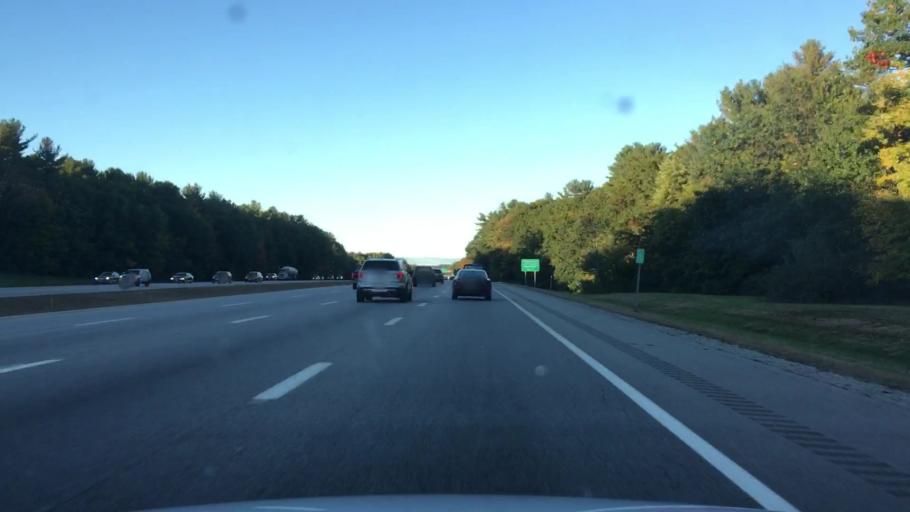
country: US
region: New Hampshire
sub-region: Rockingham County
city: Greenland
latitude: 43.0245
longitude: -70.8272
